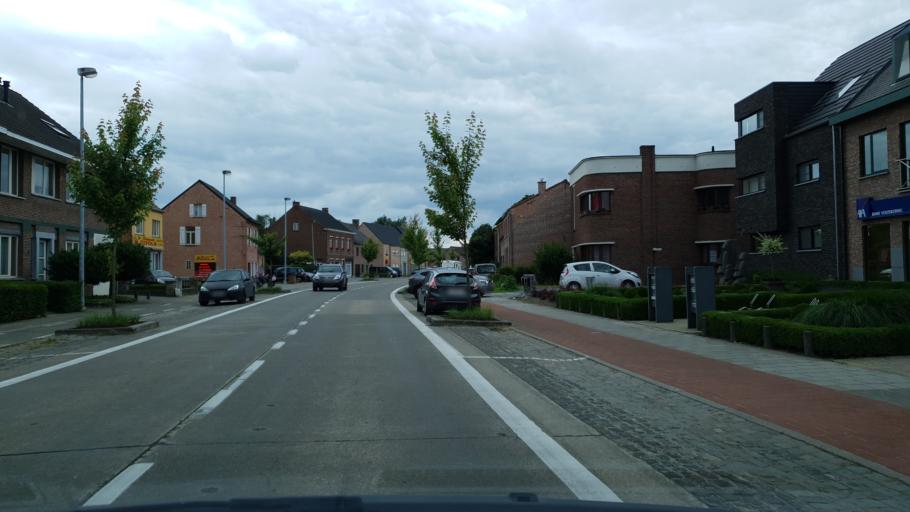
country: BE
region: Flanders
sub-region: Provincie Antwerpen
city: Hulshout
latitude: 51.0516
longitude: 4.7690
